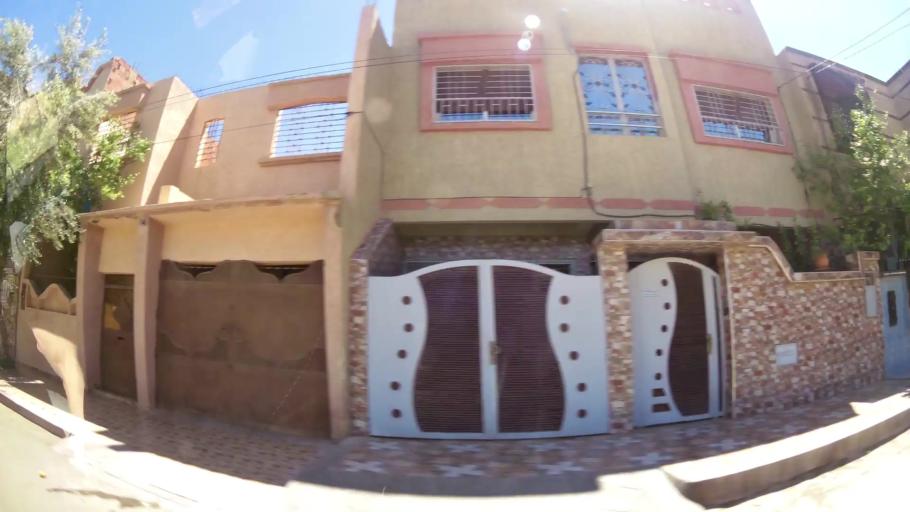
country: MA
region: Oriental
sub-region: Oujda-Angad
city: Oujda
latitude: 34.6688
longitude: -1.8834
